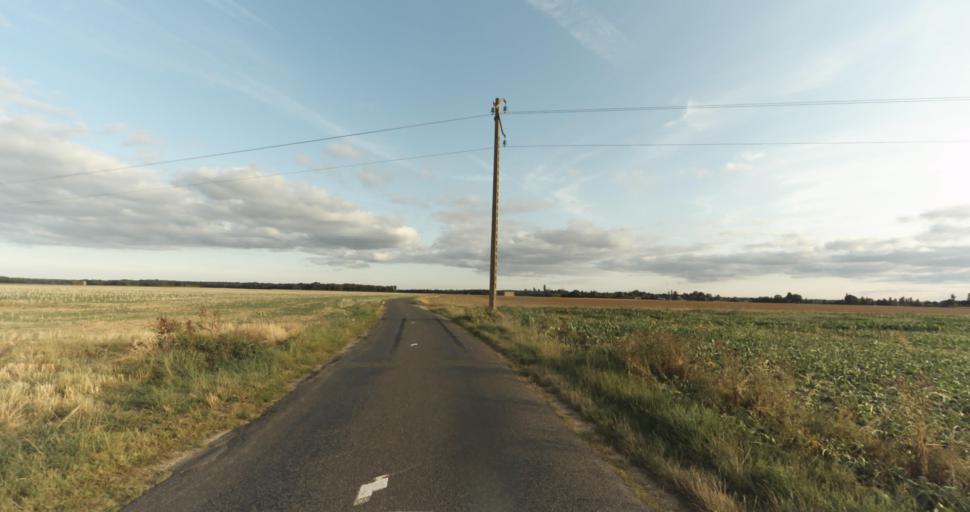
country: FR
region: Haute-Normandie
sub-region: Departement de l'Eure
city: Marcilly-sur-Eure
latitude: 48.8267
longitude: 1.2877
